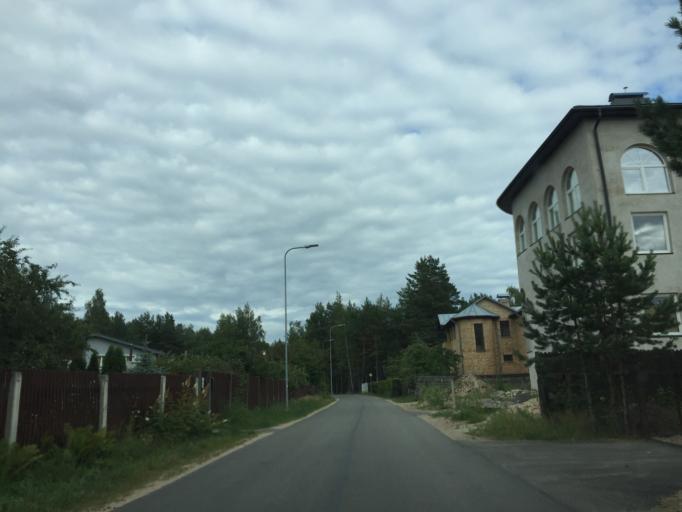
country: LV
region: Carnikava
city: Carnikava
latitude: 57.1321
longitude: 24.2536
